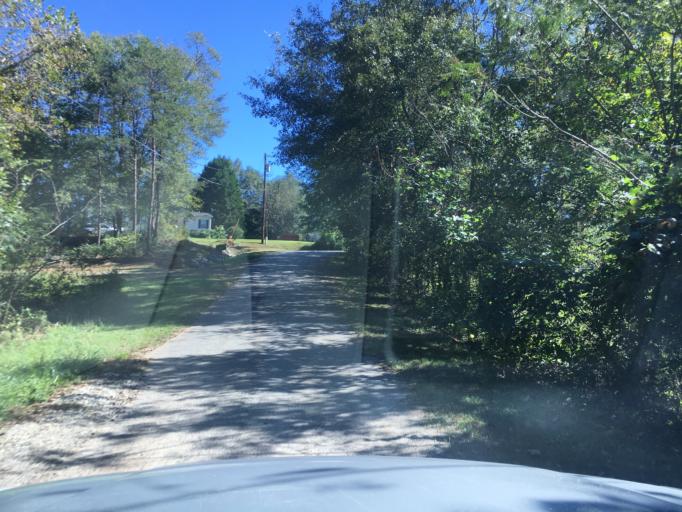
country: US
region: South Carolina
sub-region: Spartanburg County
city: Duncan
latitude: 34.9479
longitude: -82.1530
